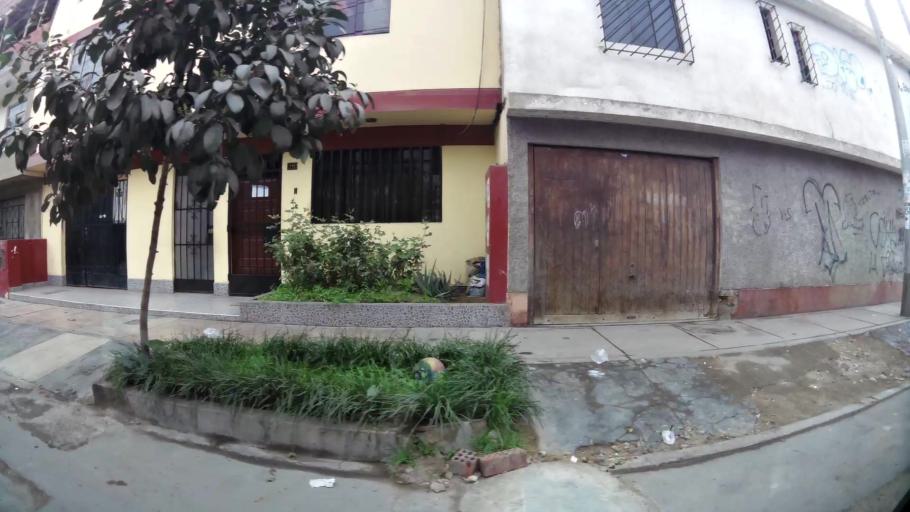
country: PE
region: Lima
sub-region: Lima
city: Independencia
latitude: -11.9714
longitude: -77.0749
